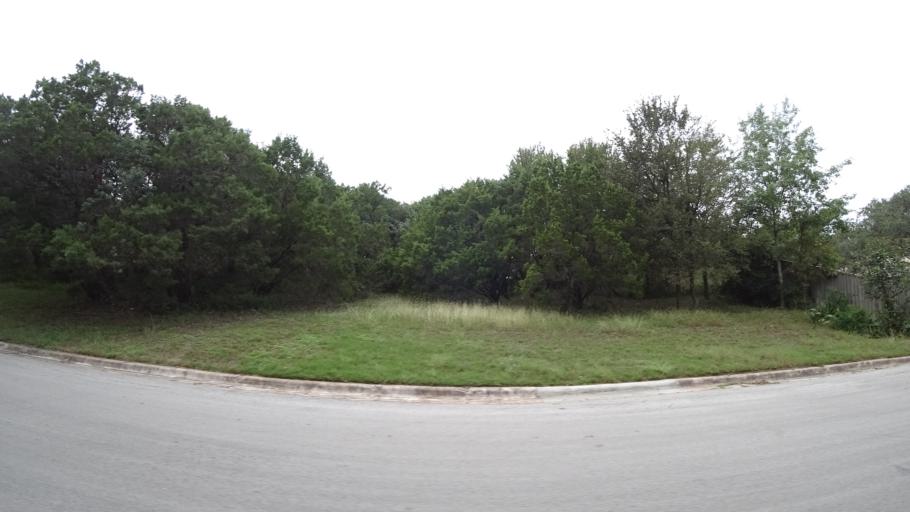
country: US
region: Texas
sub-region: Travis County
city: Rollingwood
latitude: 30.2773
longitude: -97.7932
